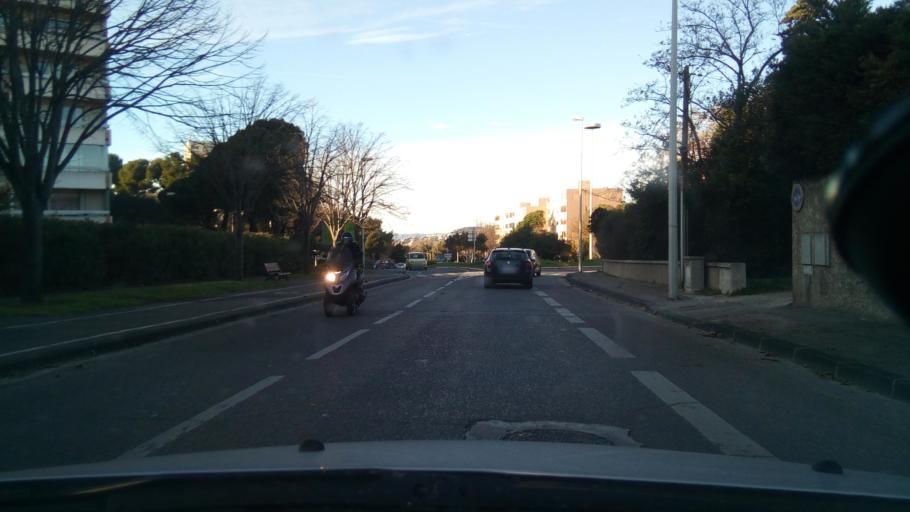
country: FR
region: Provence-Alpes-Cote d'Azur
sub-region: Departement des Bouches-du-Rhone
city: Marseille 09
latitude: 43.2452
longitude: 5.3957
